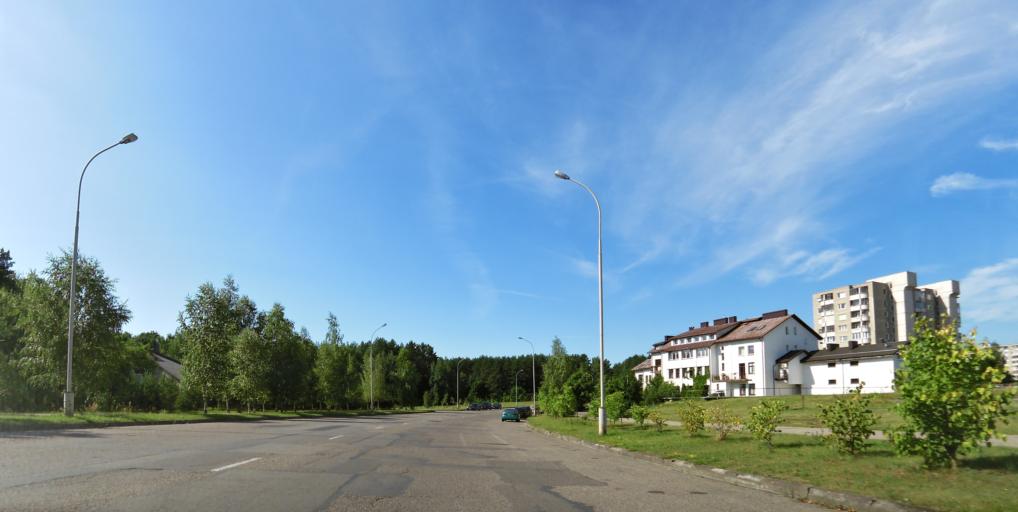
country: LT
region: Vilnius County
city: Pilaite
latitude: 54.7036
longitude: 25.1880
